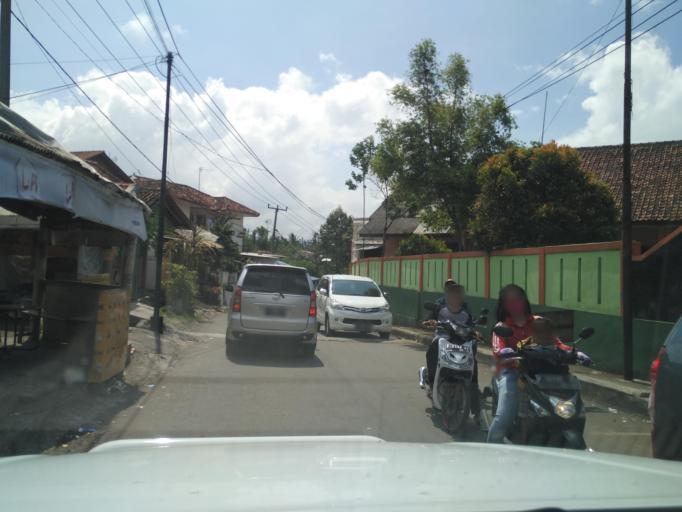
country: ID
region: West Java
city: Ciranjang-hilir
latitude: -6.7237
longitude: 107.0776
